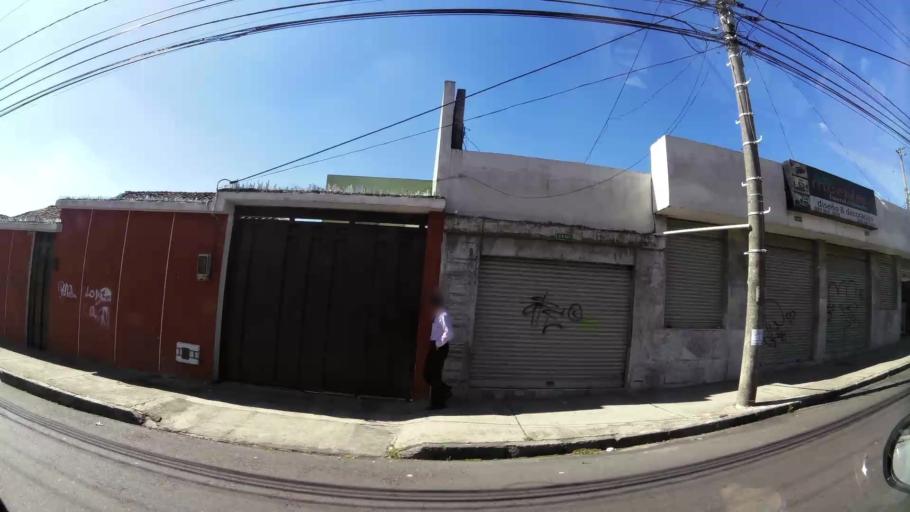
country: EC
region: Pichincha
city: Quito
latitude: -0.2421
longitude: -78.5261
